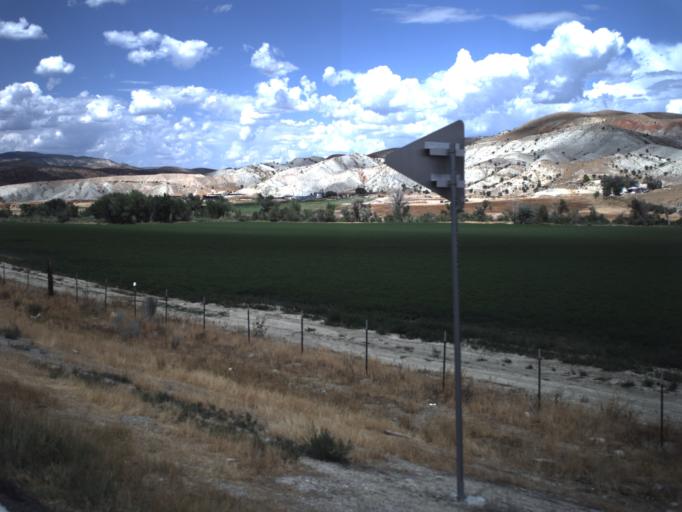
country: US
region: Utah
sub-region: Sanpete County
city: Gunnison
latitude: 39.1388
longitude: -111.7313
